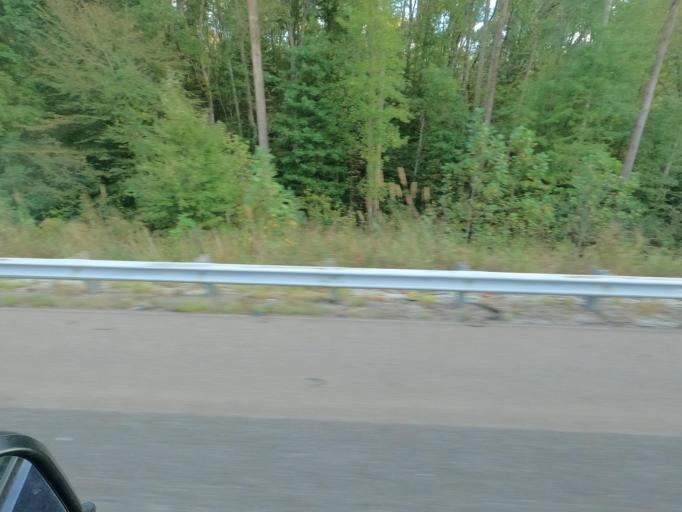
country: US
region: Tennessee
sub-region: Decatur County
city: Parsons
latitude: 35.8173
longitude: -88.1881
